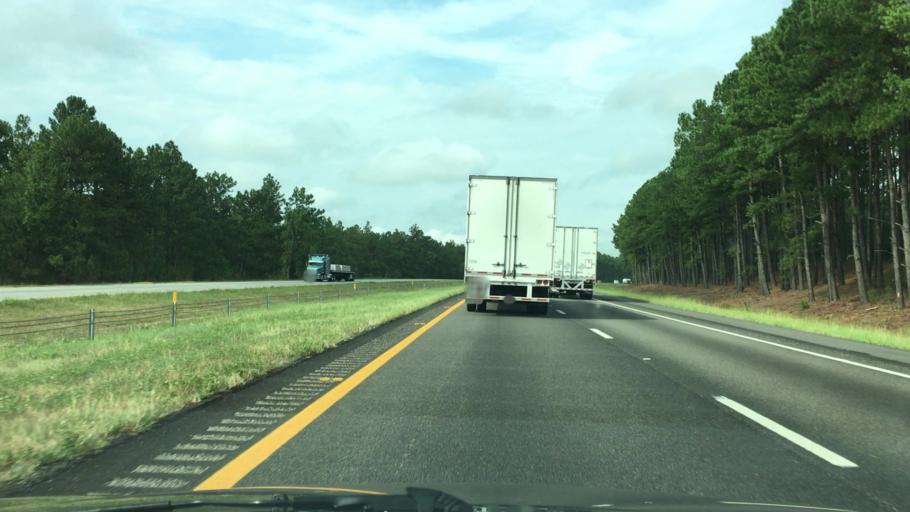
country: US
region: South Carolina
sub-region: Aiken County
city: Aiken
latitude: 33.6864
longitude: -81.6191
